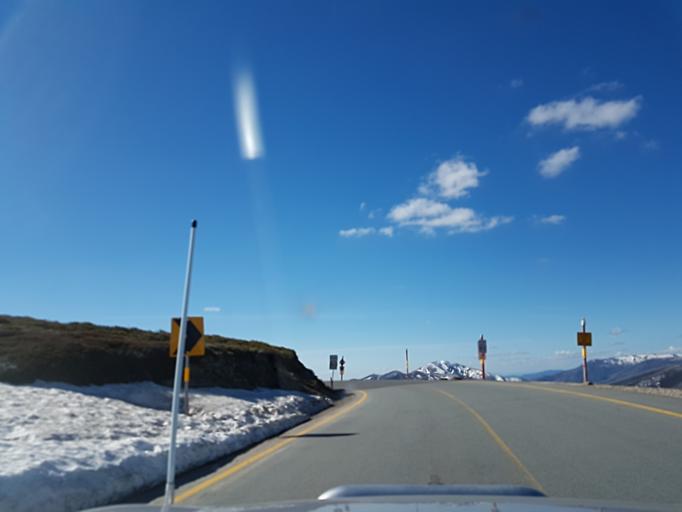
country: AU
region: Victoria
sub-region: Alpine
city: Mount Beauty
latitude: -36.9753
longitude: 147.1327
